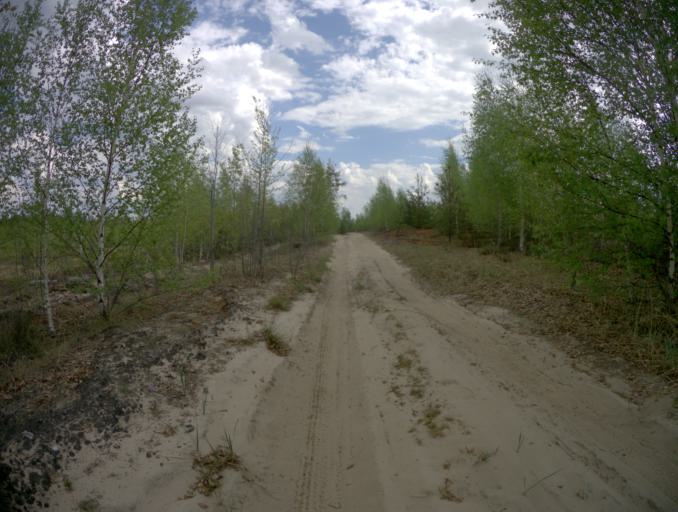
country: RU
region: Ivanovo
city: Talitsy
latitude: 56.4606
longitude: 42.2300
